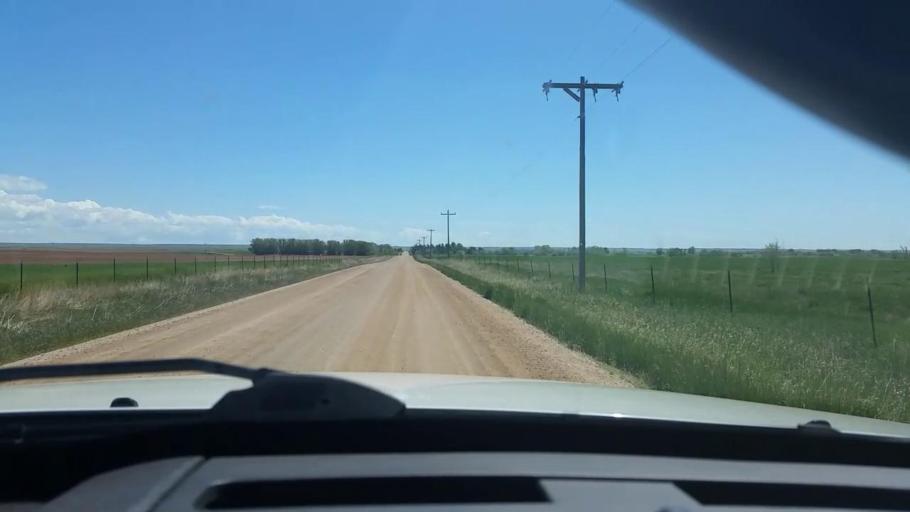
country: US
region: Colorado
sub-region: Larimer County
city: Wellington
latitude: 40.7982
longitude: -105.0756
